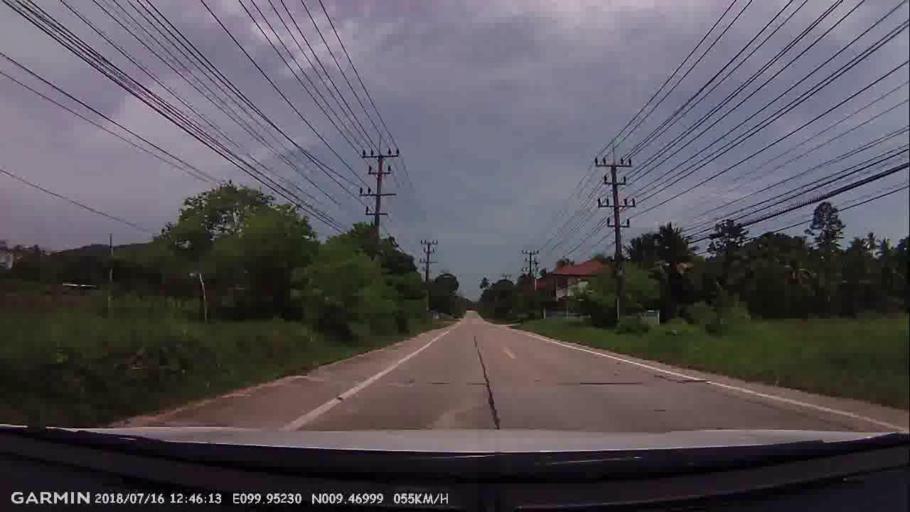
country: TH
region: Surat Thani
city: Ko Samui
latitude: 9.4699
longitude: 99.9523
